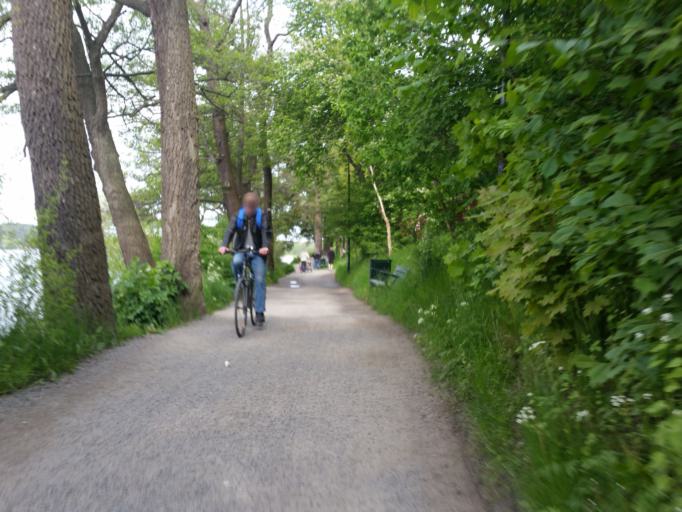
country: SE
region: Stockholm
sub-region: Stockholms Kommun
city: Arsta
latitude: 59.3052
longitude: 18.0637
